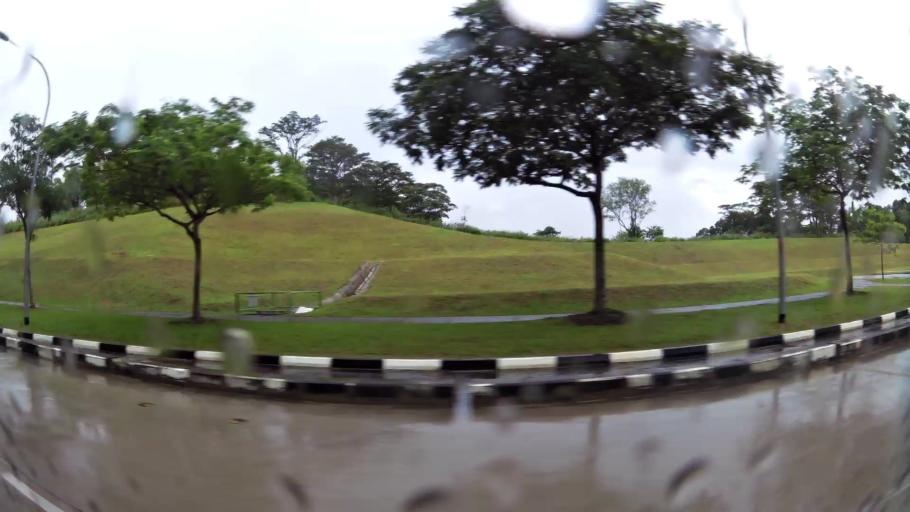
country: MY
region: Johor
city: Kampung Pasir Gudang Baru
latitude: 1.3985
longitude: 103.8789
